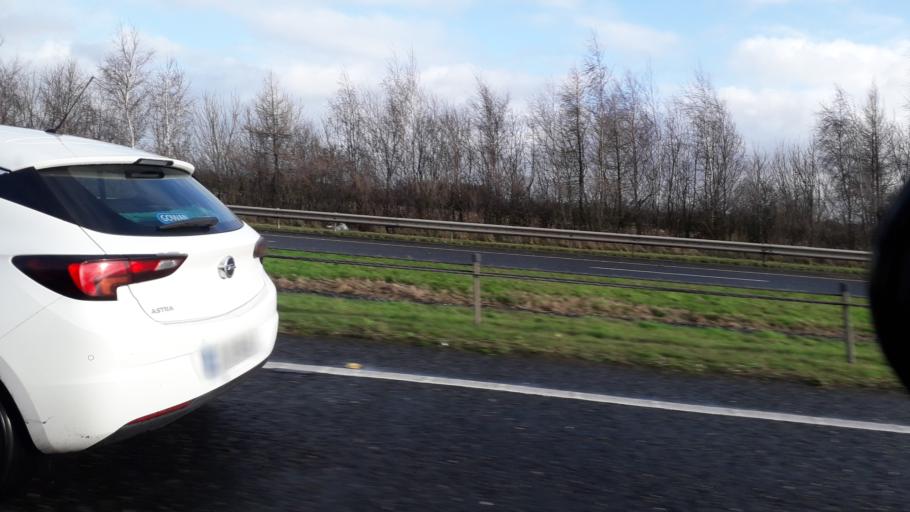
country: IE
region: Leinster
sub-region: Fingal County
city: Blanchardstown
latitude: 53.4524
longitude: -6.3549
